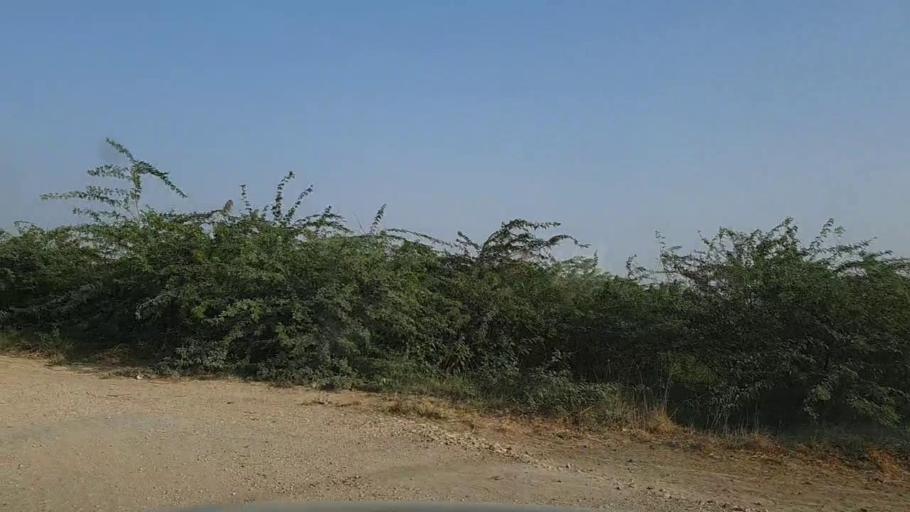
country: PK
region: Sindh
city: Mirpur Sakro
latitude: 24.5873
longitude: 67.6491
